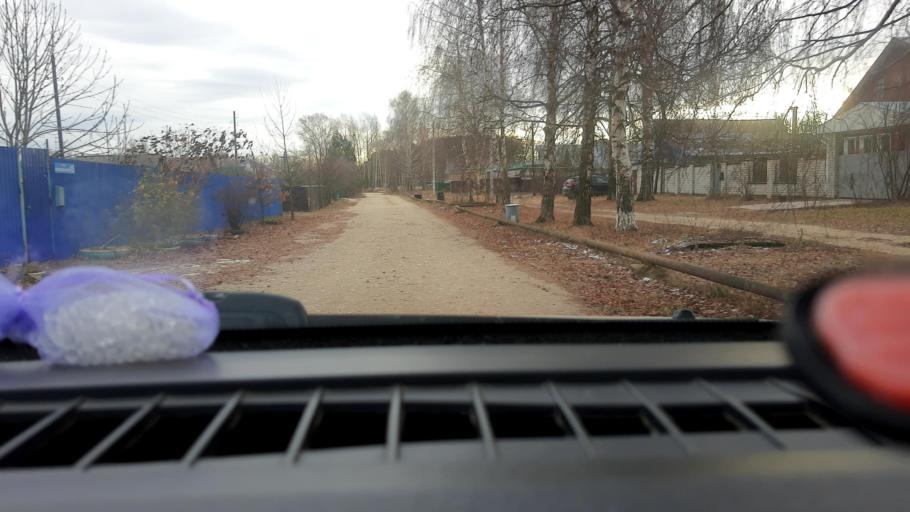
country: RU
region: Nizjnij Novgorod
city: Gorbatovka
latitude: 56.3822
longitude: 43.7743
